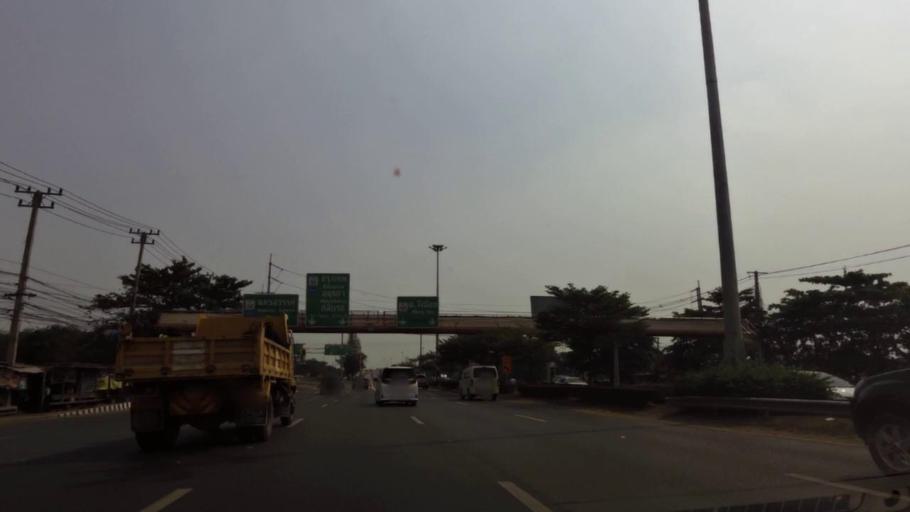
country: TH
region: Phra Nakhon Si Ayutthaya
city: Phra Nakhon Si Ayutthaya
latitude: 14.3436
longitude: 100.6099
